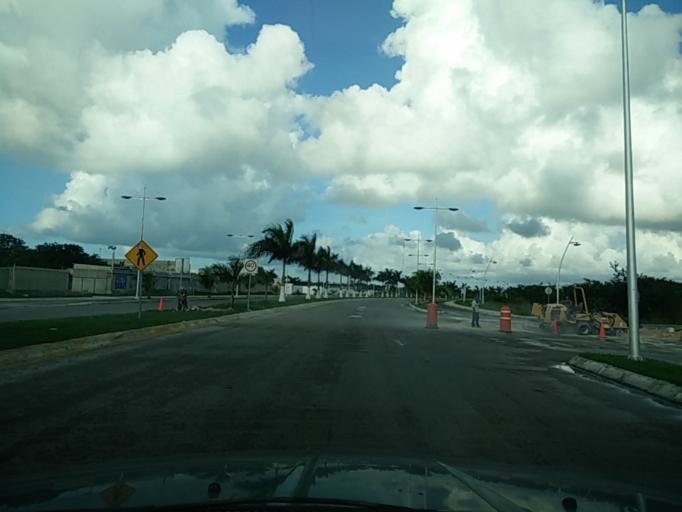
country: MX
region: Quintana Roo
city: San Miguel de Cozumel
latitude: 20.4911
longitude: -86.9334
